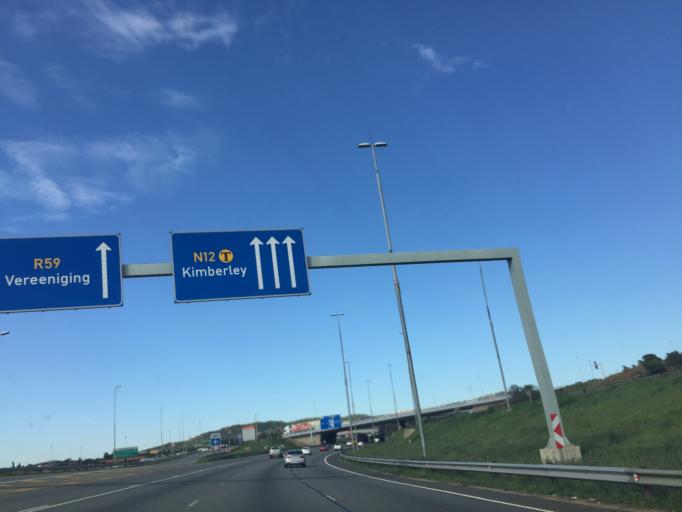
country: ZA
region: Gauteng
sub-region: Ekurhuleni Metropolitan Municipality
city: Germiston
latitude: -26.2570
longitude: 28.1200
